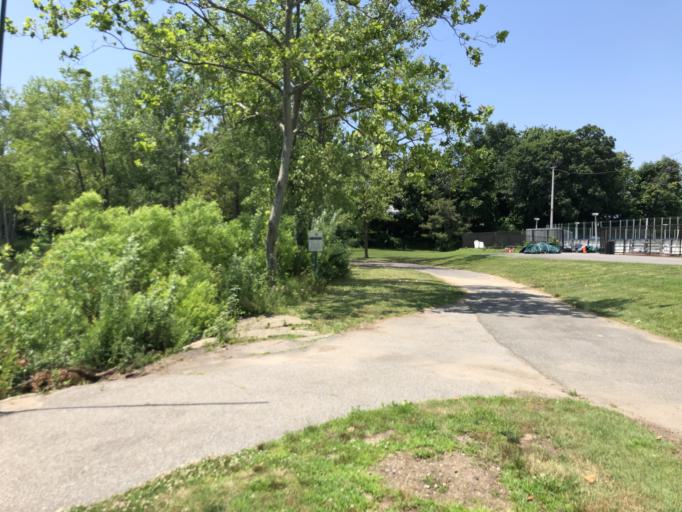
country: US
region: New York
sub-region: Nassau County
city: Hewlett
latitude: 40.6438
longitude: -73.6886
